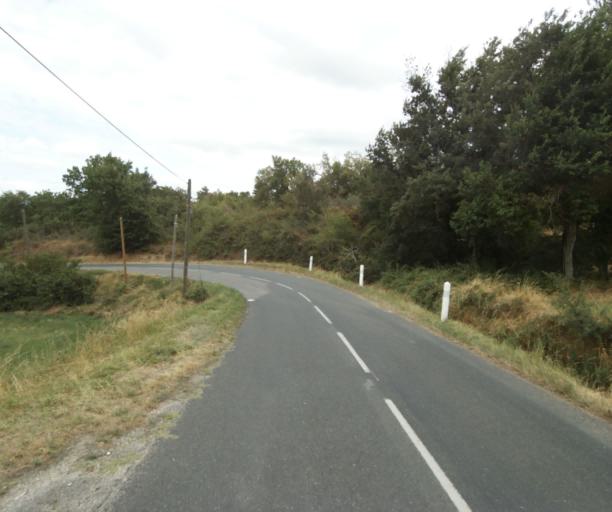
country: FR
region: Midi-Pyrenees
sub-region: Departement de la Haute-Garonne
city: Revel
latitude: 43.4422
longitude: 1.9874
